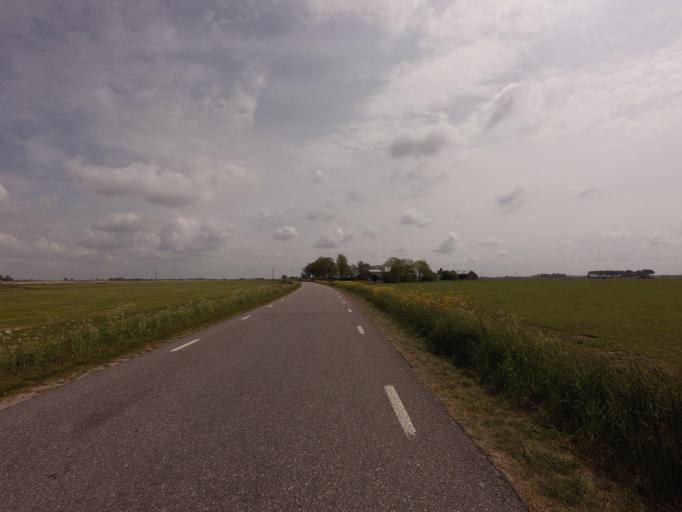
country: NL
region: Friesland
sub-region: Sudwest Fryslan
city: Bolsward
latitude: 53.1080
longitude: 5.4939
